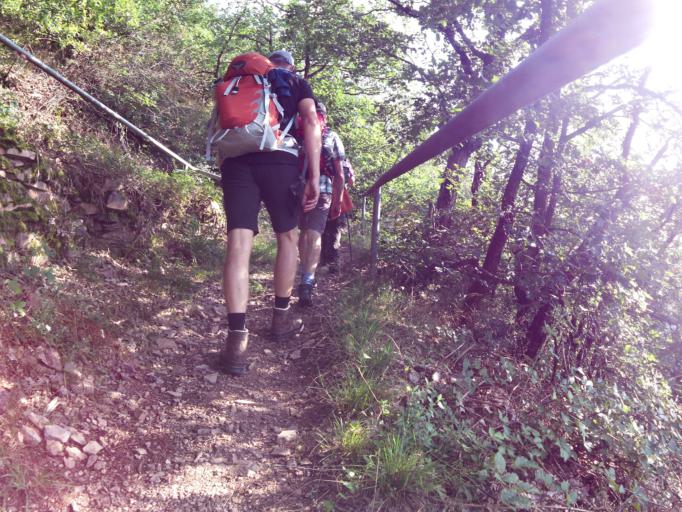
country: DE
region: Rheinland-Pfalz
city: Bad Munster am Stein-Ebernburg
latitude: 49.8172
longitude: 7.8438
